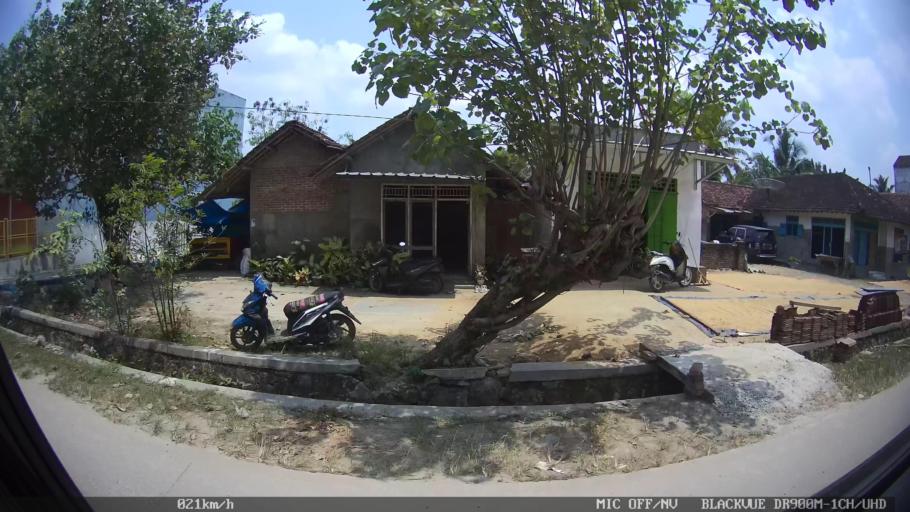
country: ID
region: Lampung
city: Pringsewu
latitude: -5.3587
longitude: 104.9952
